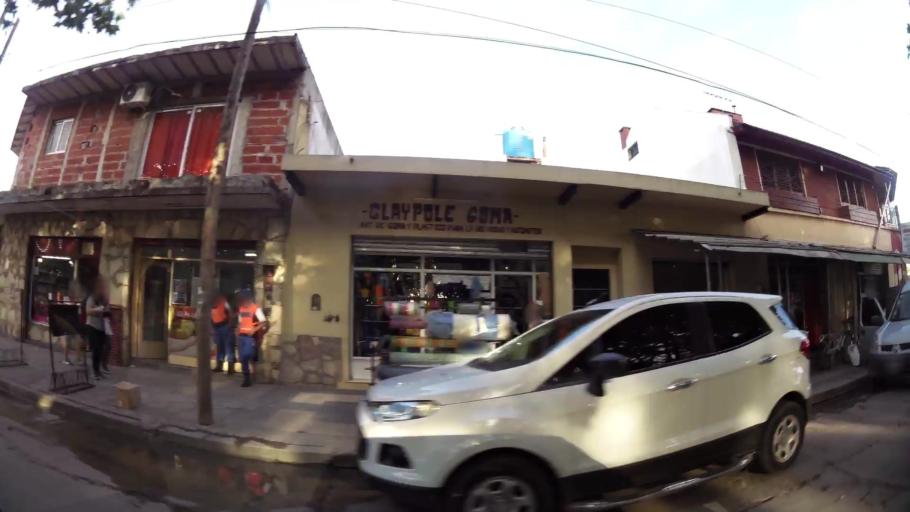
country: AR
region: Buenos Aires
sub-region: Partido de Almirante Brown
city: Adrogue
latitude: -34.7973
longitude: -58.3347
